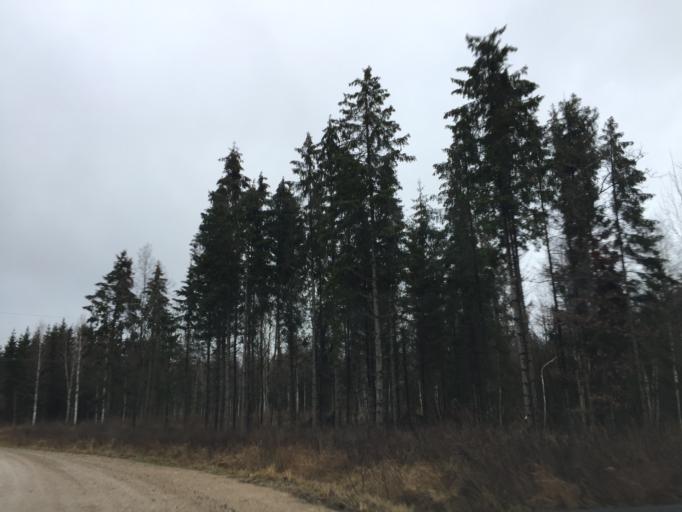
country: LV
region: Saldus Rajons
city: Saldus
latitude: 56.6703
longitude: 22.4029
